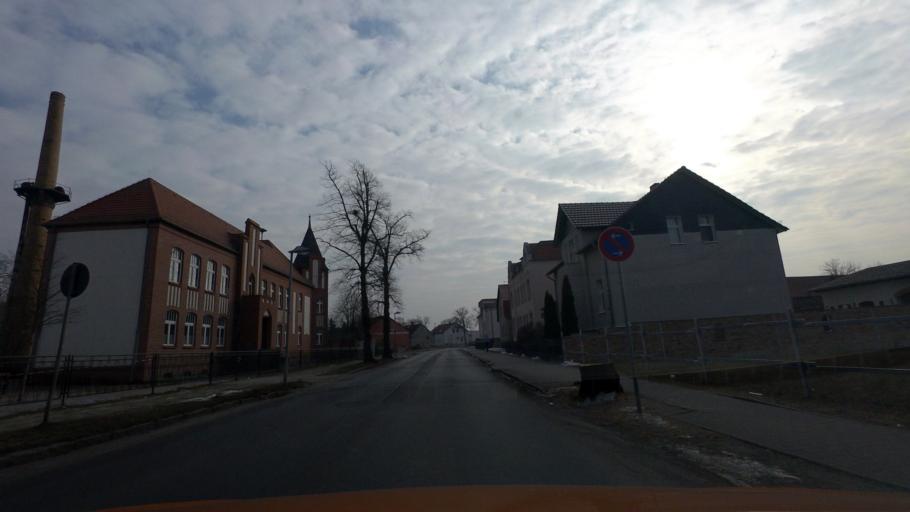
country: DE
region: Brandenburg
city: Zossen
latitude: 52.2409
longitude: 13.4315
